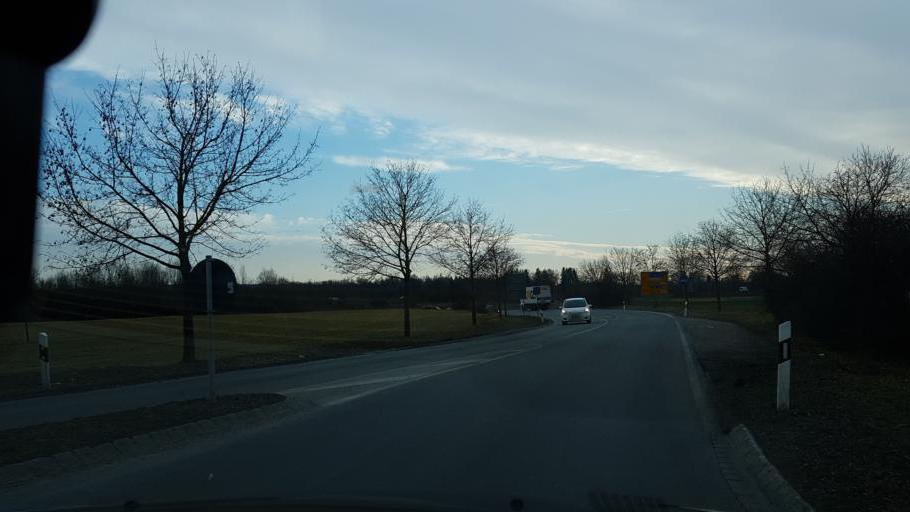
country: DE
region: Bavaria
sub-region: Upper Bavaria
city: Fuerstenfeldbruck
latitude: 48.1869
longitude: 11.2349
